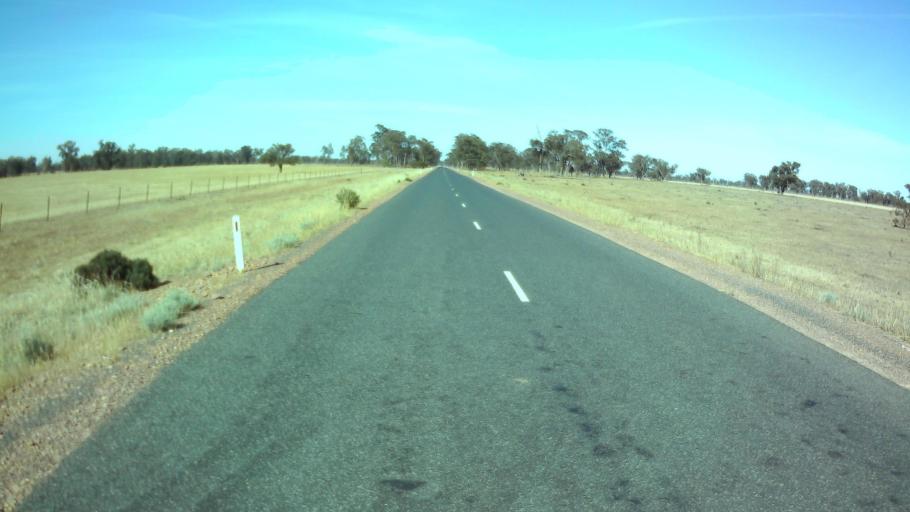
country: AU
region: New South Wales
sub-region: Weddin
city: Grenfell
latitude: -34.0993
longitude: 147.8795
